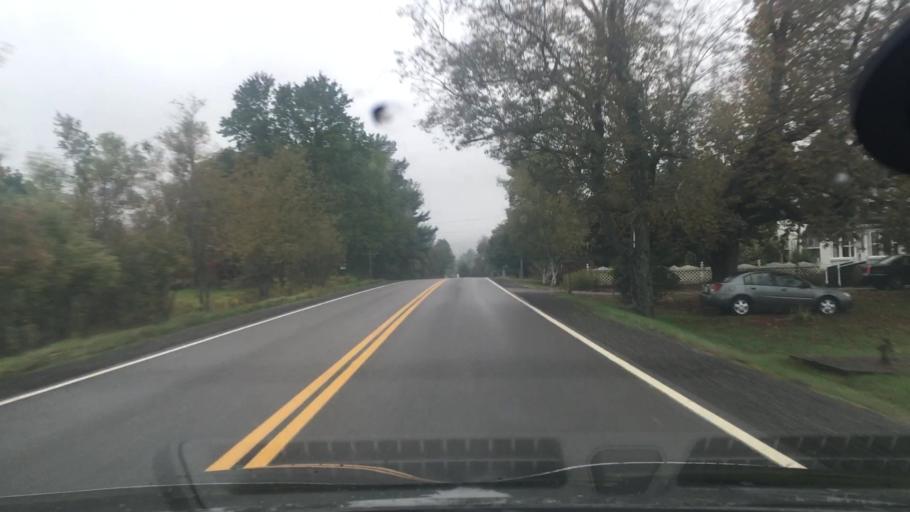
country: CA
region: Nova Scotia
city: Windsor
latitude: 44.9391
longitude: -64.1903
